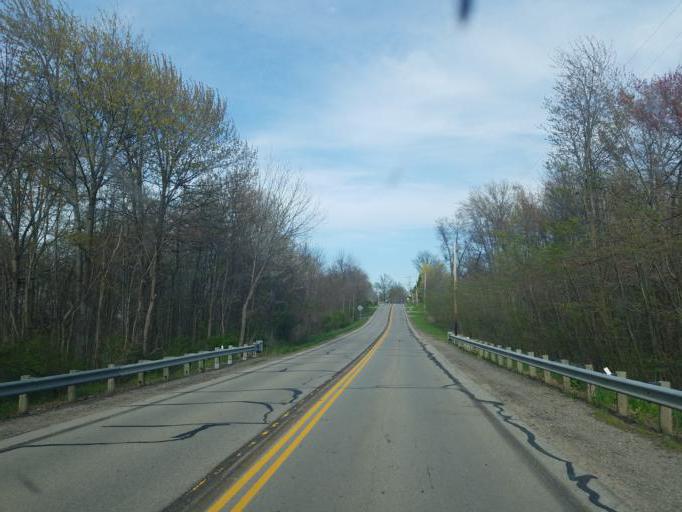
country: US
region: Ohio
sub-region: Ashtabula County
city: Geneva-on-the-Lake
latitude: 41.8650
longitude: -80.9195
